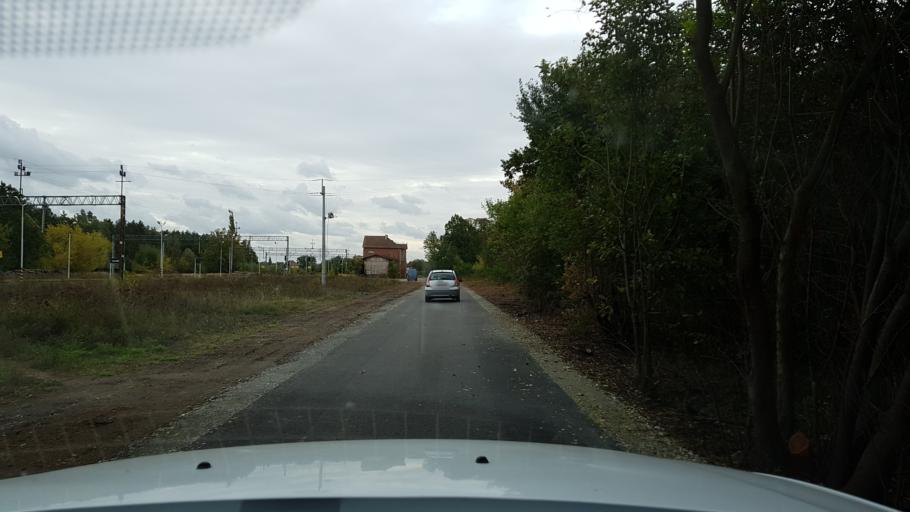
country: PL
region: West Pomeranian Voivodeship
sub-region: Powiat gryfinski
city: Chojna
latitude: 52.9025
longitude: 14.4577
